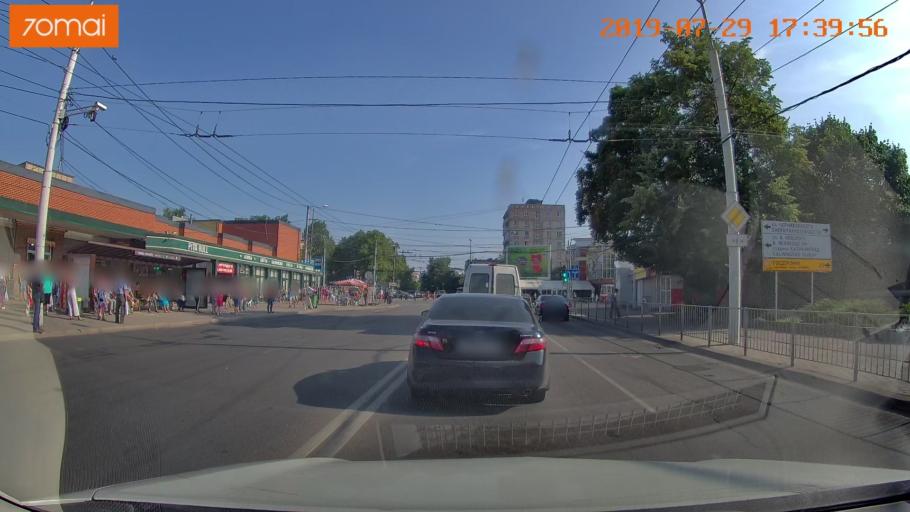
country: RU
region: Kaliningrad
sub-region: Gorod Kaliningrad
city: Kaliningrad
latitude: 54.7205
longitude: 20.5076
